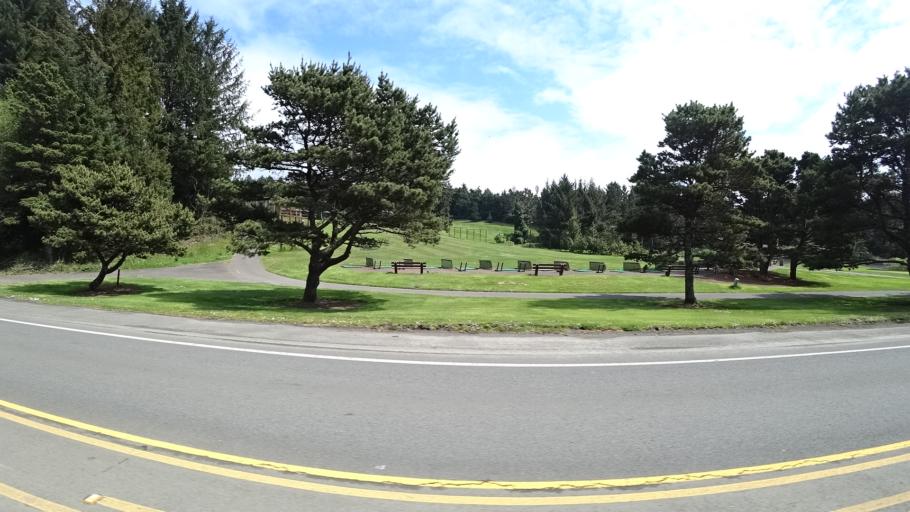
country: US
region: Oregon
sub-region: Lincoln County
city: Lincoln Beach
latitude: 44.8884
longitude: -124.0260
